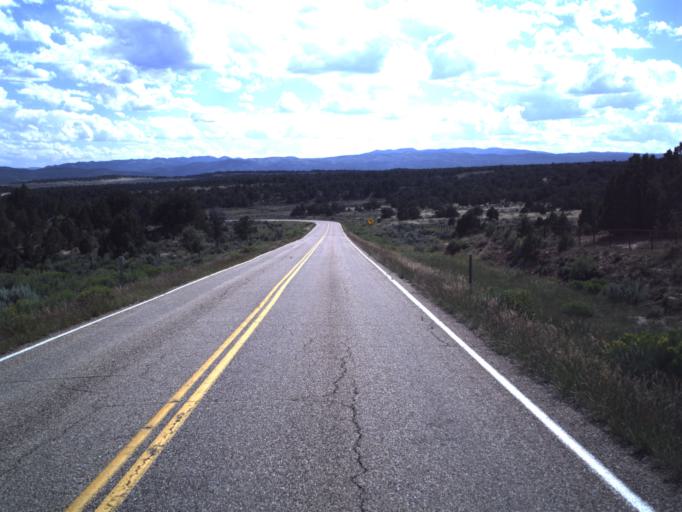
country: US
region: Utah
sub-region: Duchesne County
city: Duchesne
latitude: 40.2833
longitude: -110.7007
